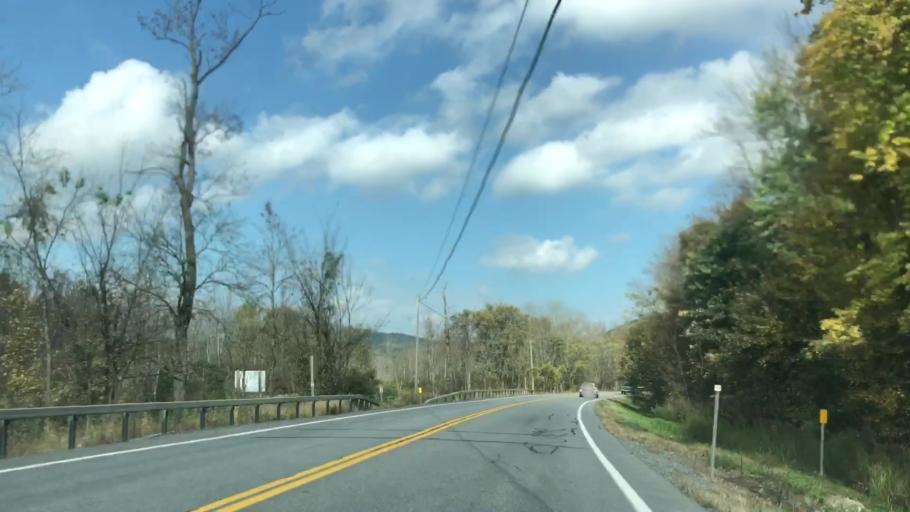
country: US
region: New York
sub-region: Warren County
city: Queensbury
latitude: 43.4211
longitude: -73.4856
